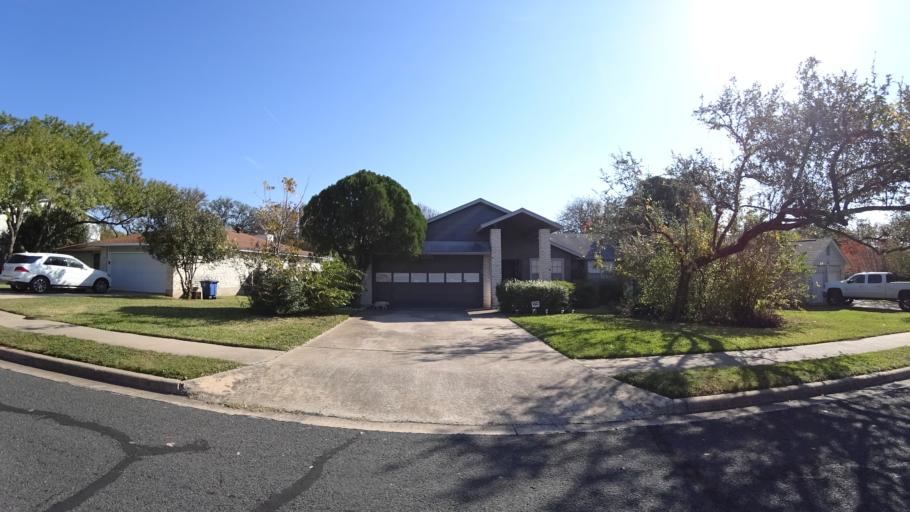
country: US
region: Texas
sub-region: Travis County
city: Barton Creek
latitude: 30.2297
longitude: -97.8499
